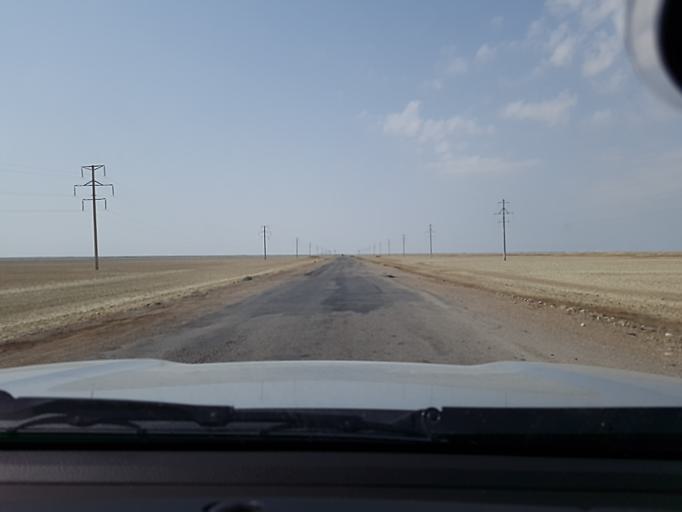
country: TM
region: Balkan
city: Gumdag
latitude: 39.0715
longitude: 54.5843
